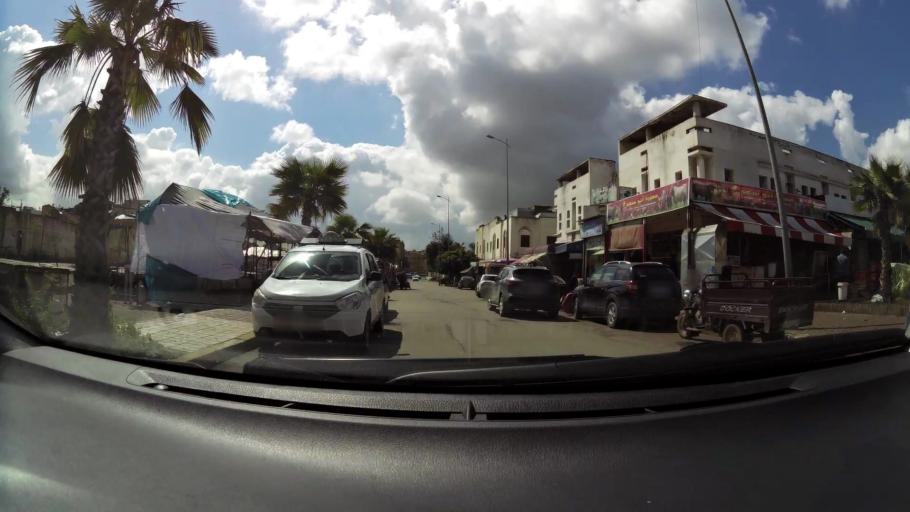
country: MA
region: Grand Casablanca
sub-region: Mediouna
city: Tit Mellil
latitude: 33.5503
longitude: -7.4866
